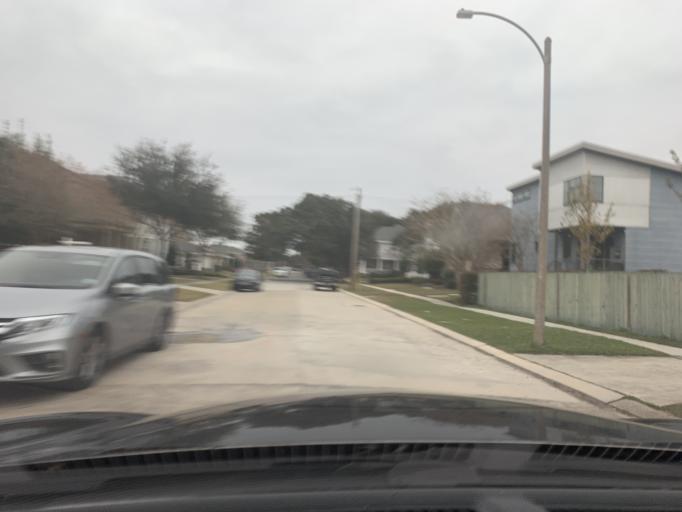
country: US
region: Louisiana
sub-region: Jefferson Parish
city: Metairie
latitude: 30.0168
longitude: -90.1054
